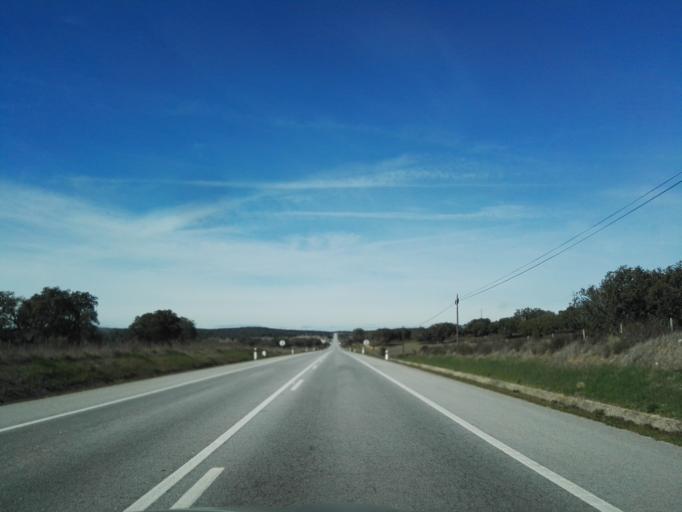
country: PT
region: Portalegre
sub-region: Arronches
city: Arronches
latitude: 39.1520
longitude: -7.3121
